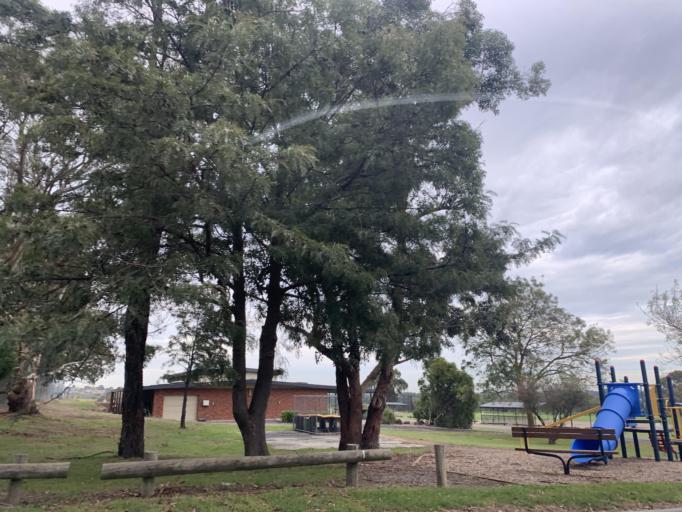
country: AU
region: Victoria
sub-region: Knox
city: Rowville
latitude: -37.9574
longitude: 145.2392
